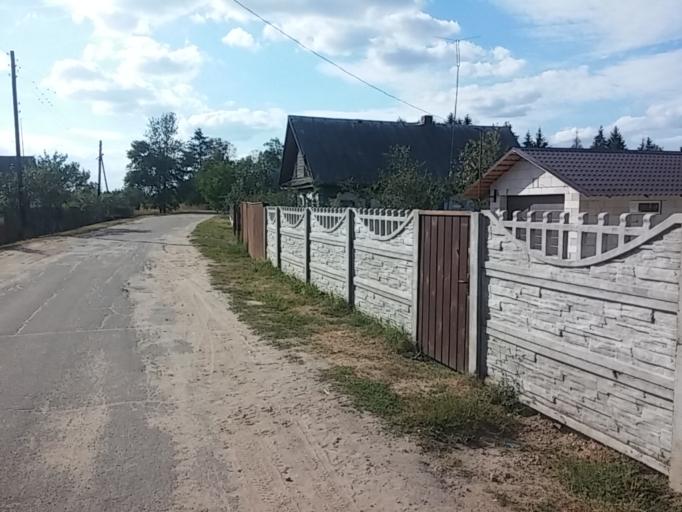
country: BY
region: Minsk
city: Chervyen'
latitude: 53.7769
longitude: 28.2581
